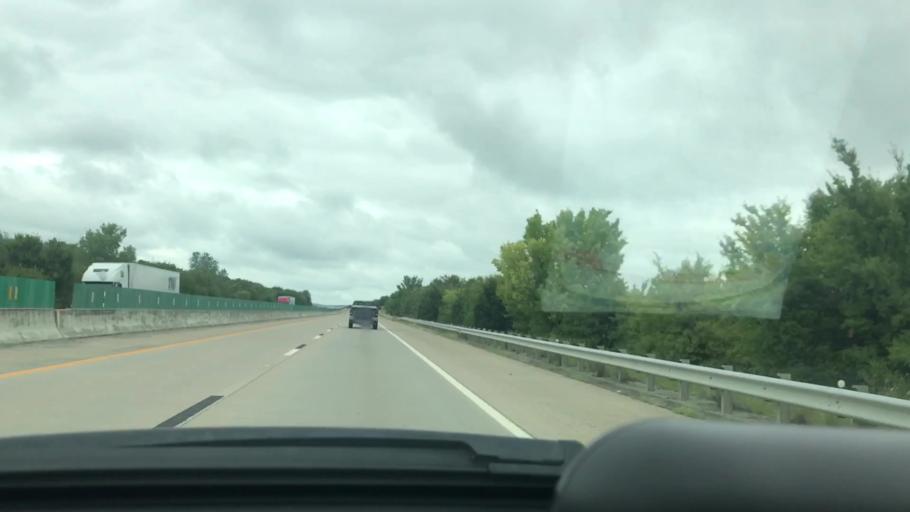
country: US
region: Oklahoma
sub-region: Pittsburg County
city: Krebs
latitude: 35.0285
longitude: -95.7146
